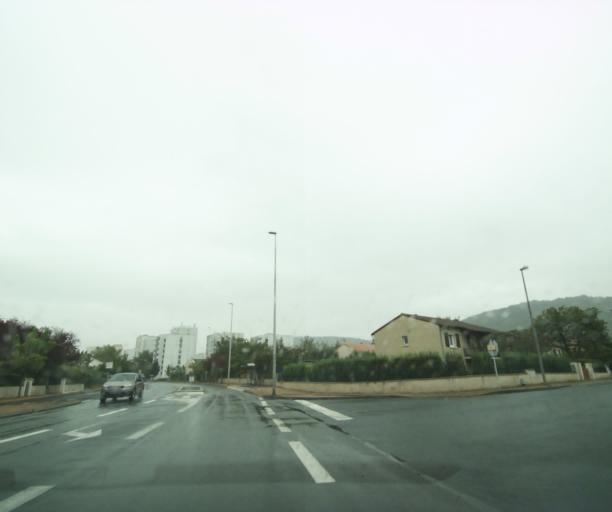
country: FR
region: Auvergne
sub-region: Departement du Puy-de-Dome
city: Cebazat
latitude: 45.8181
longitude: 3.1073
